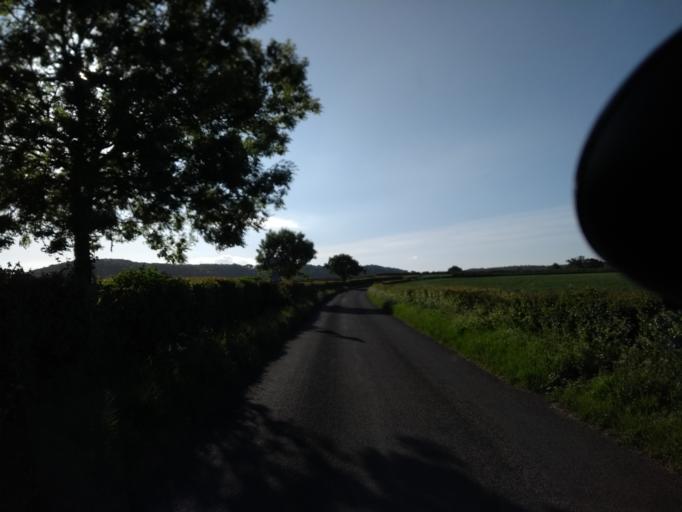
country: GB
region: England
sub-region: Somerset
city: Taunton
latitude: 51.0004
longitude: -3.0696
